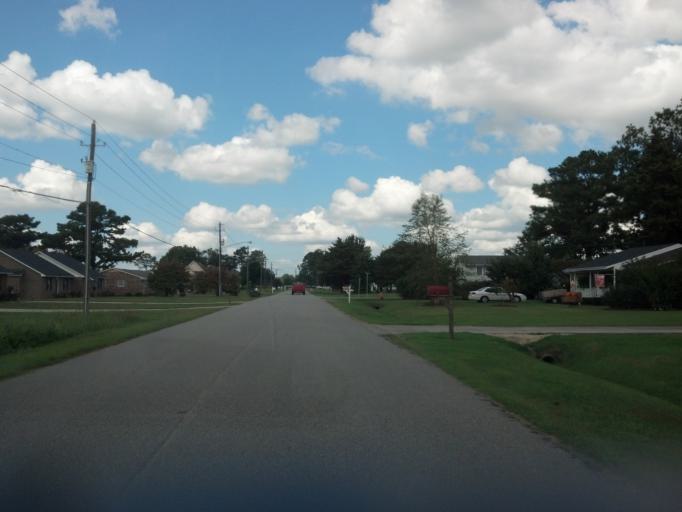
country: US
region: North Carolina
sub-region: Pitt County
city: Ayden
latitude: 35.4773
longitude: -77.4095
